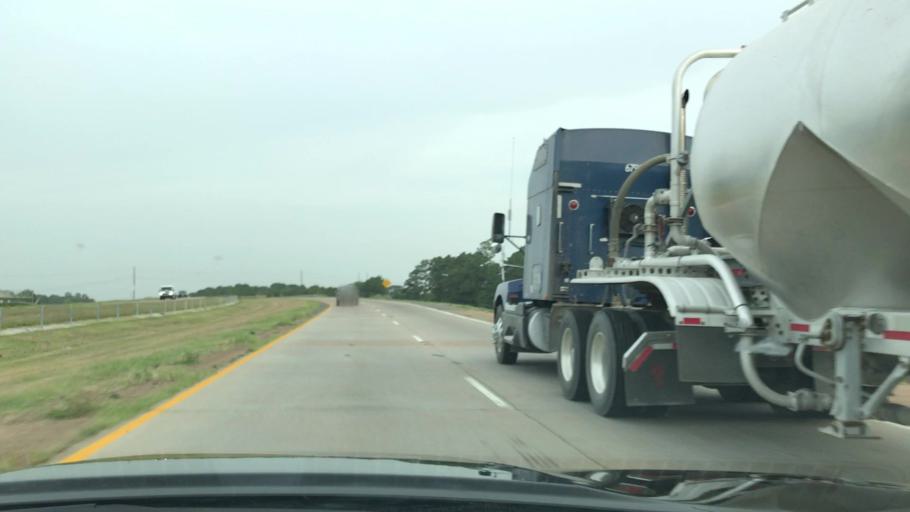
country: US
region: Louisiana
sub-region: Bossier Parish
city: Bossier City
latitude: 32.4170
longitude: -93.7937
